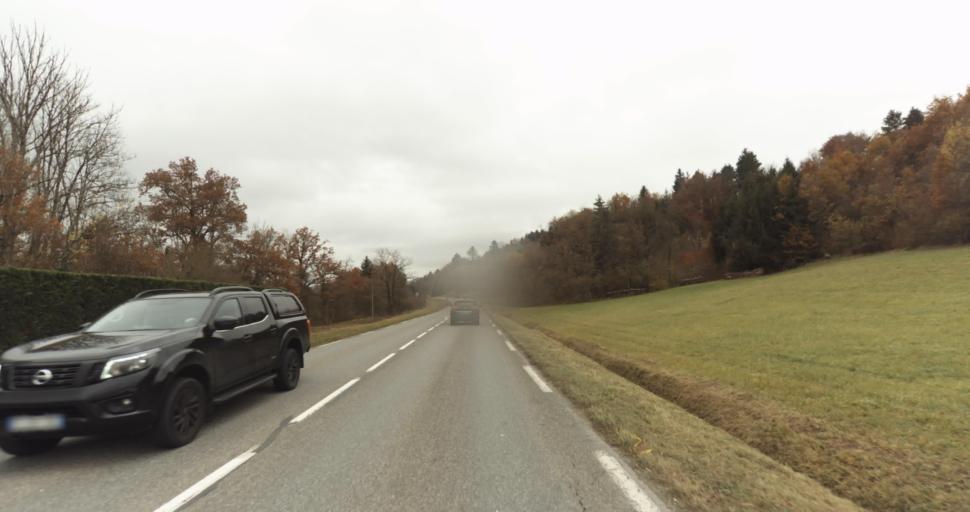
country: FR
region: Rhone-Alpes
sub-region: Departement de la Haute-Savoie
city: Groisy
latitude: 45.9974
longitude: 6.1768
